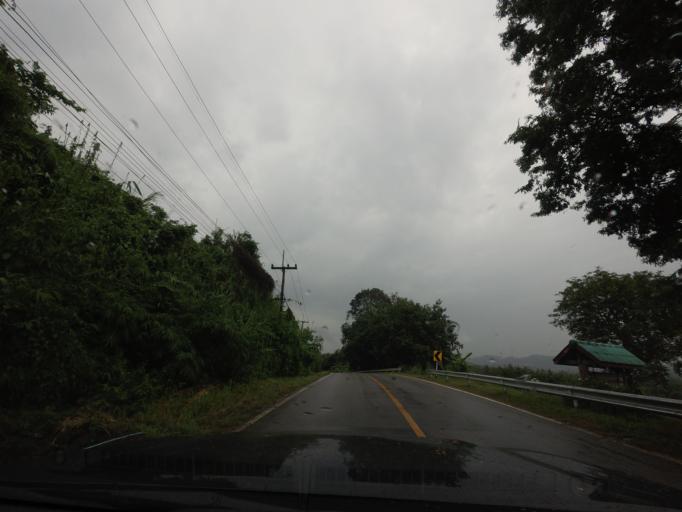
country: TH
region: Nong Khai
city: Sangkhom
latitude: 18.1819
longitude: 102.1695
